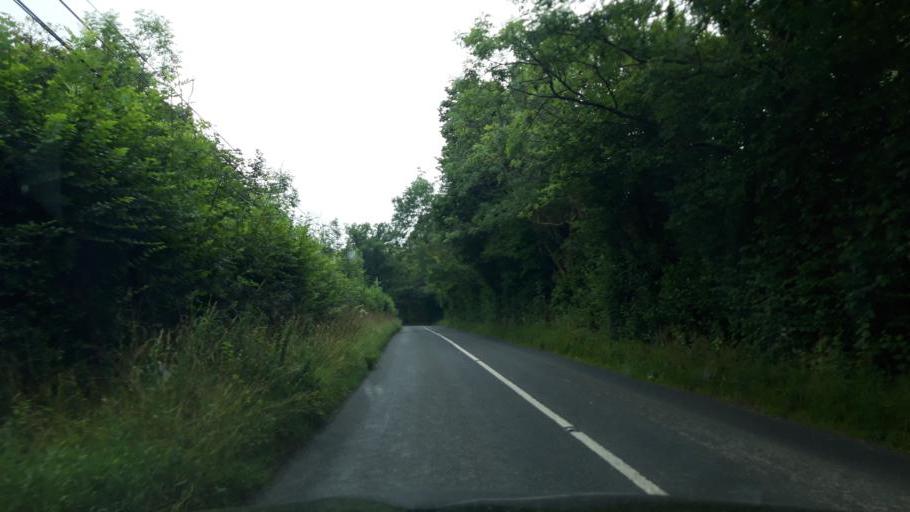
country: IE
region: Munster
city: Fethard
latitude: 52.5365
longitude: -7.6816
